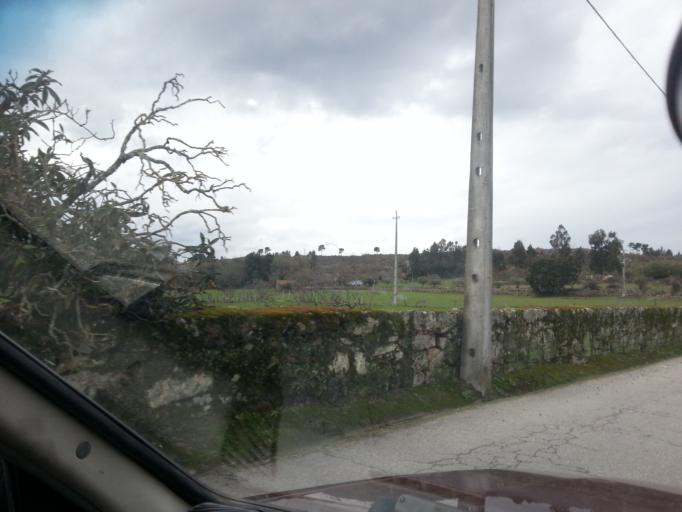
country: PT
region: Guarda
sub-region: Fornos de Algodres
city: Fornos de Algodres
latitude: 40.5891
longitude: -7.4924
